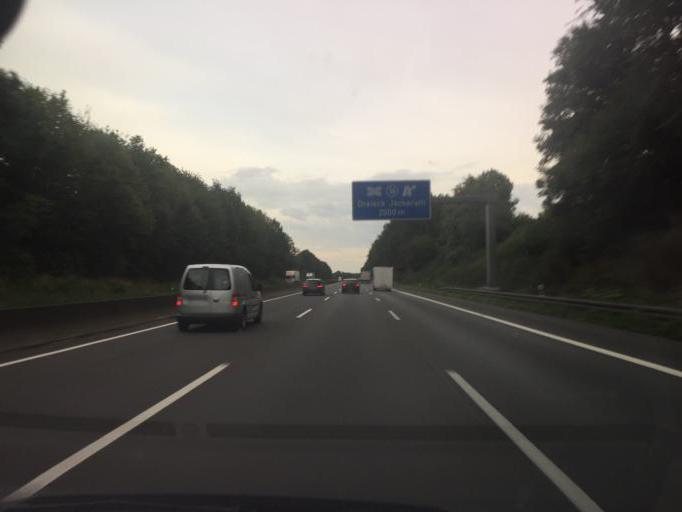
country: DE
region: North Rhine-Westphalia
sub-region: Regierungsbezirk Koln
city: Titz
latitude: 51.0637
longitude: 6.4374
